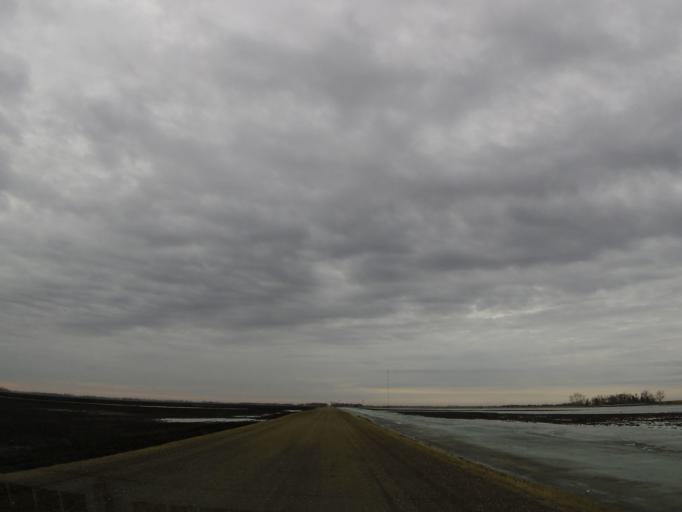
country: US
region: North Dakota
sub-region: Walsh County
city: Grafton
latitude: 48.4043
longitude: -97.4483
